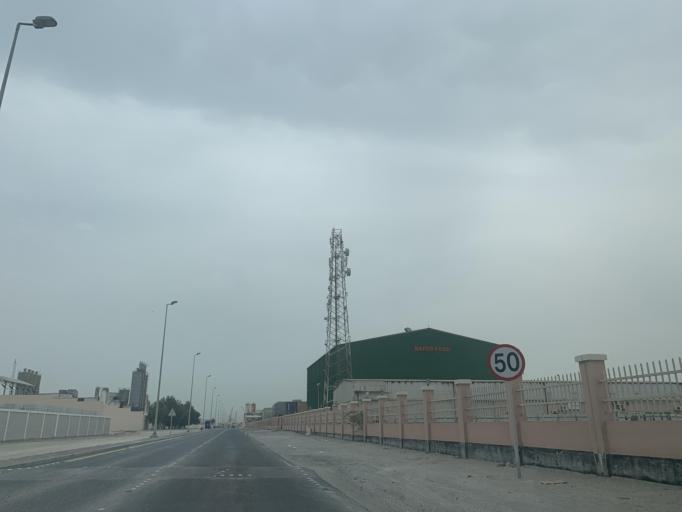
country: BH
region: Muharraq
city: Al Hadd
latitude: 26.2107
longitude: 50.6616
